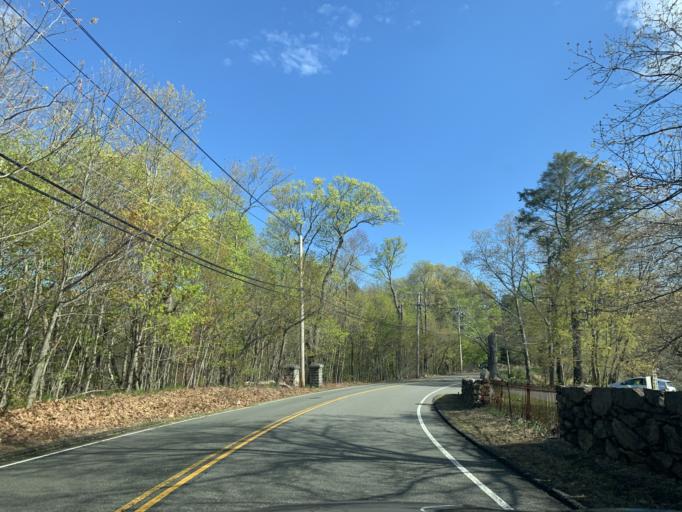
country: US
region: Massachusetts
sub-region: Norfolk County
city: Milton
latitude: 42.2297
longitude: -71.1122
